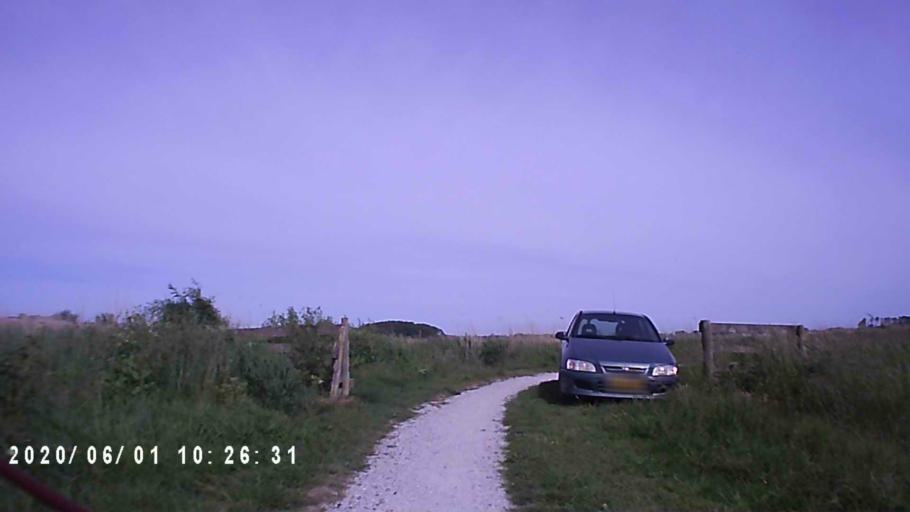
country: NL
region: Friesland
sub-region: Gemeente Het Bildt
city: Minnertsga
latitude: 53.2337
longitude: 5.6187
